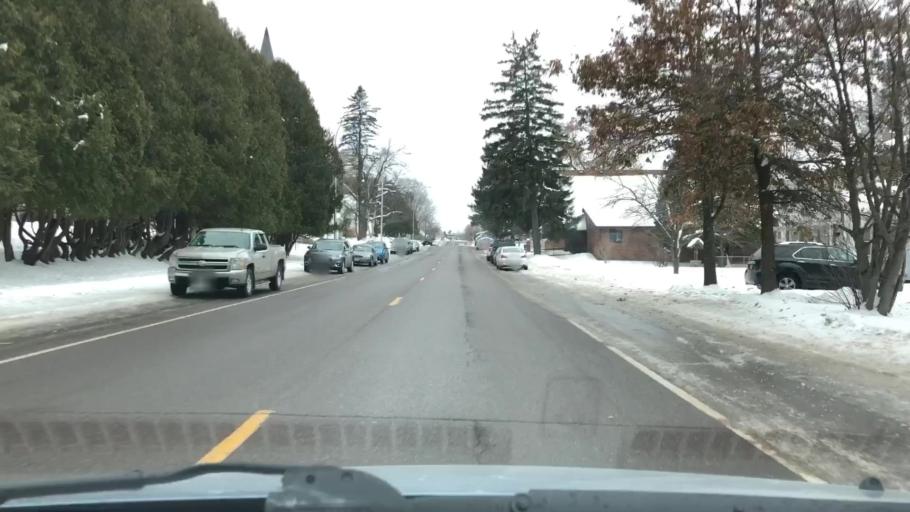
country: US
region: Minnesota
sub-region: Carlton County
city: Carlton
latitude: 46.6640
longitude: -92.4188
